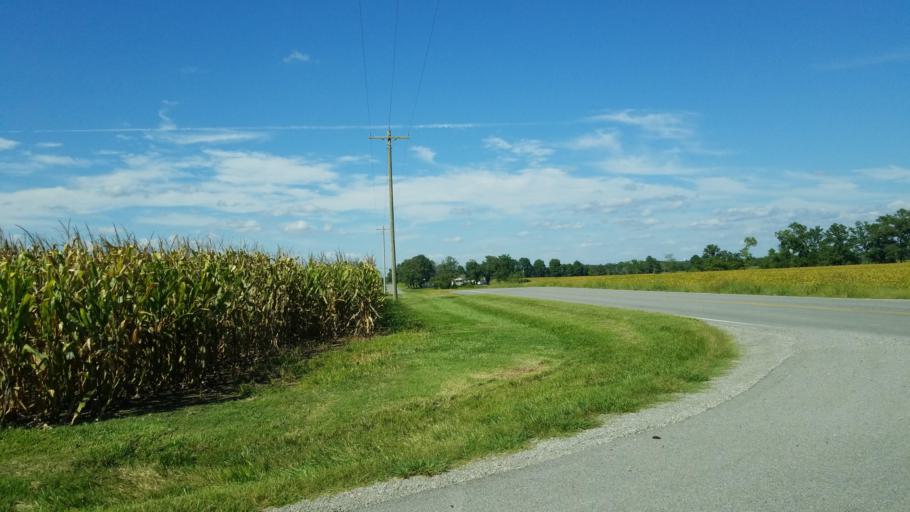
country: US
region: Illinois
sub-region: Williamson County
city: Johnston City
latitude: 37.7868
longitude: -88.7762
